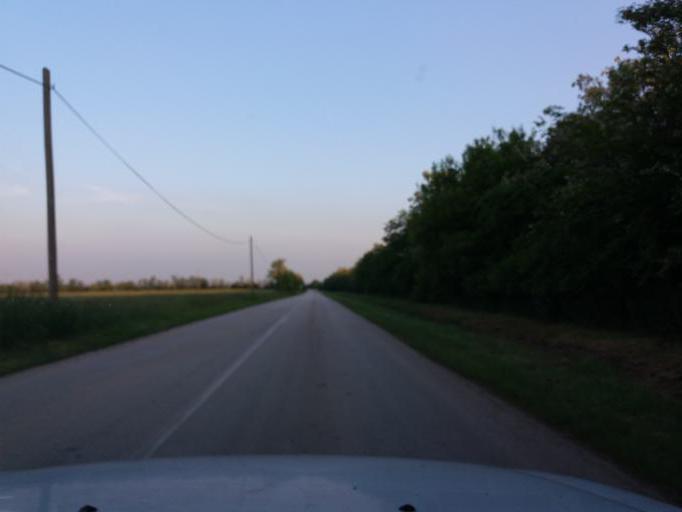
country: HU
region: Pest
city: Soskut
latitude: 47.3898
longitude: 18.7919
